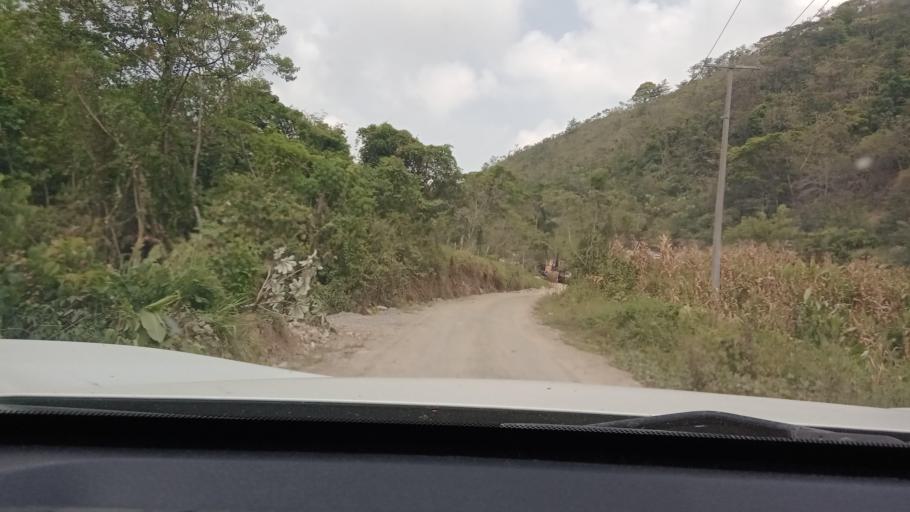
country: MX
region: Tabasco
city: Chontalpa
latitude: 17.4930
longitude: -93.6619
